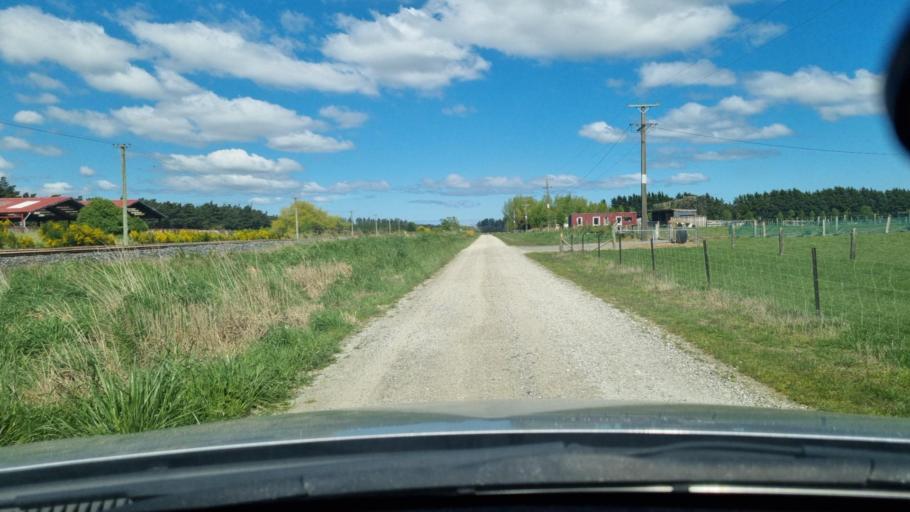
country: NZ
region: Southland
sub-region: Invercargill City
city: Invercargill
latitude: -46.3465
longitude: 168.3401
